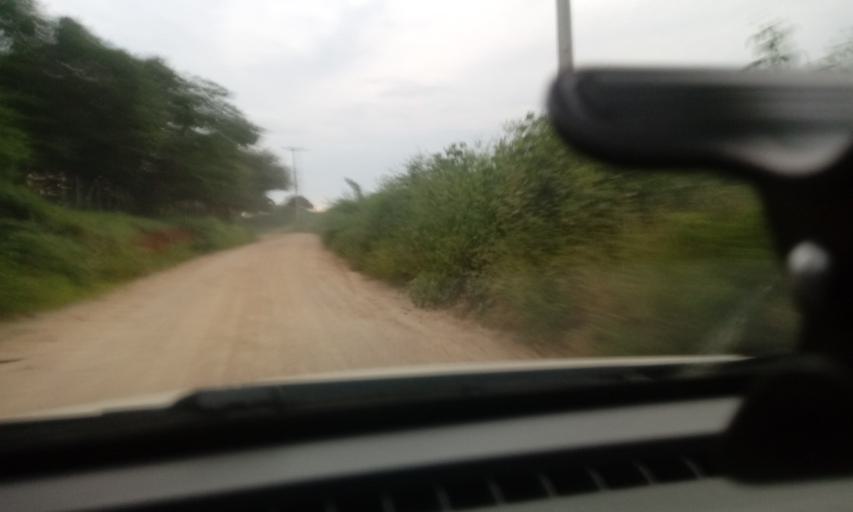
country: BR
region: Bahia
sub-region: Riacho De Santana
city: Riacho de Santana
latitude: -13.8068
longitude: -42.7568
